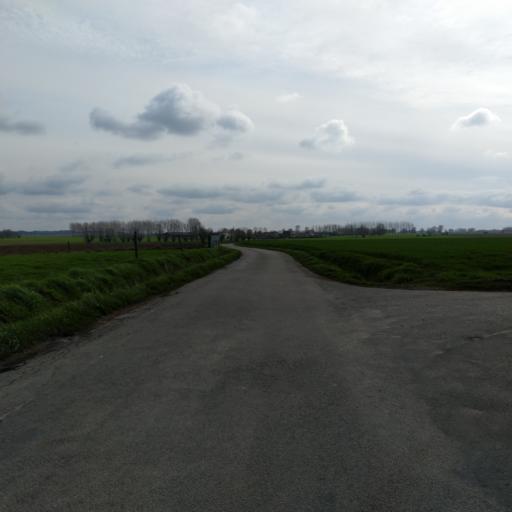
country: BE
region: Wallonia
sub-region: Province du Hainaut
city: Soignies
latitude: 50.5573
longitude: 4.0637
